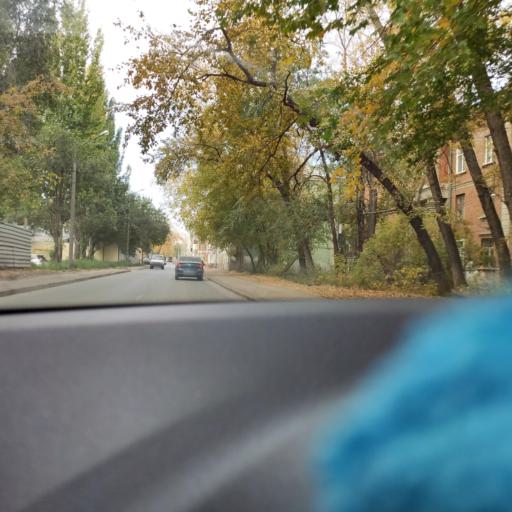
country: RU
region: Samara
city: Samara
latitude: 53.2158
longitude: 50.2637
